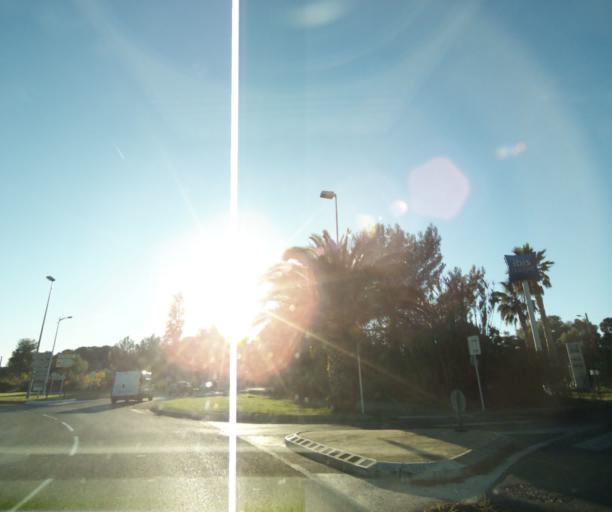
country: FR
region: Provence-Alpes-Cote d'Azur
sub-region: Departement du Var
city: Saint-Cyr-sur-Mer
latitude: 43.1838
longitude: 5.6907
